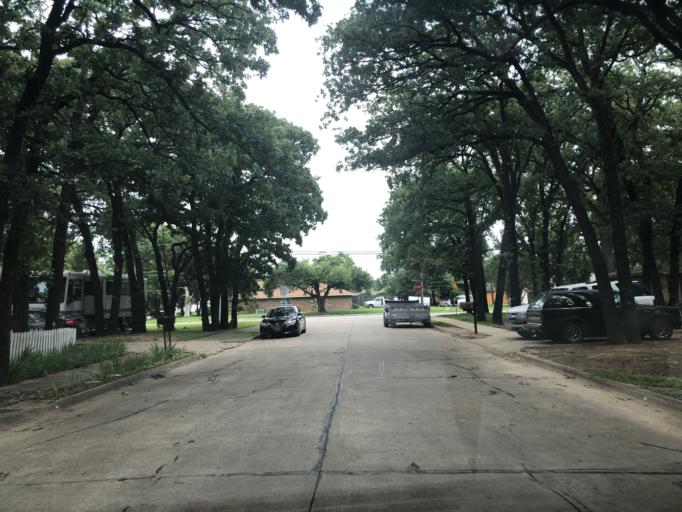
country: US
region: Texas
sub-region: Dallas County
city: Irving
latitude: 32.8004
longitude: -96.9819
